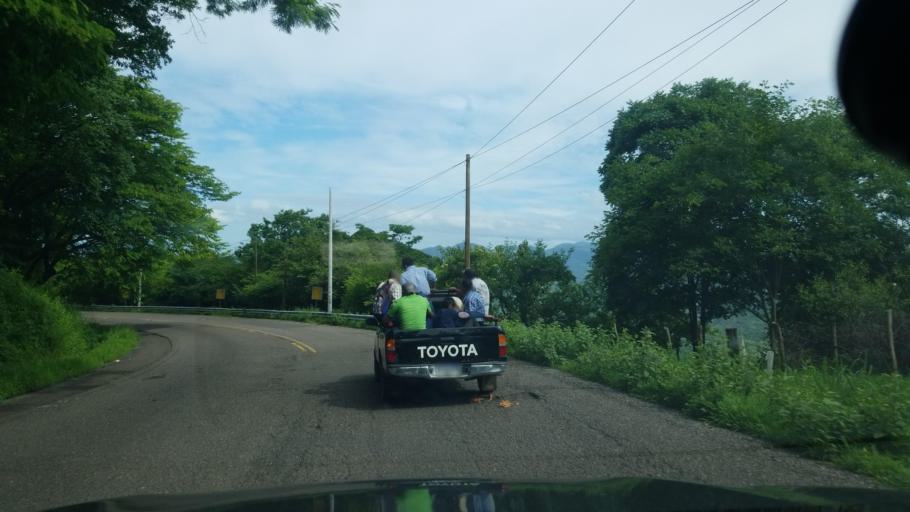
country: HN
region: Choluteca
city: Corpus
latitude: 13.3747
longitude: -87.0488
